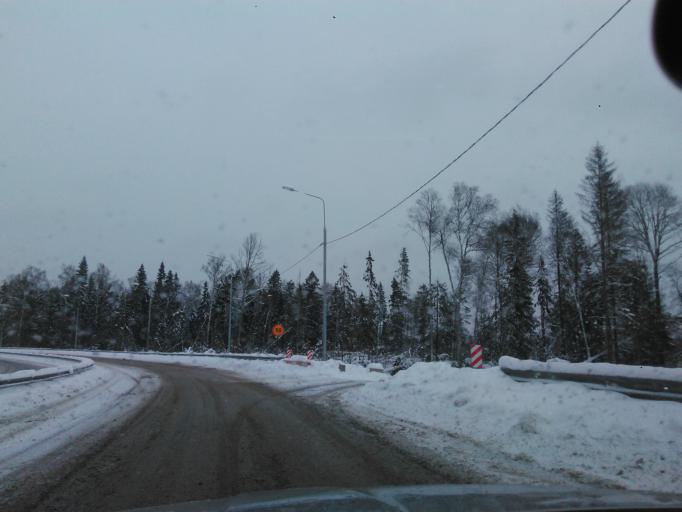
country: RU
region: Moskovskaya
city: Povarovo
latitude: 56.0052
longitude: 37.0289
